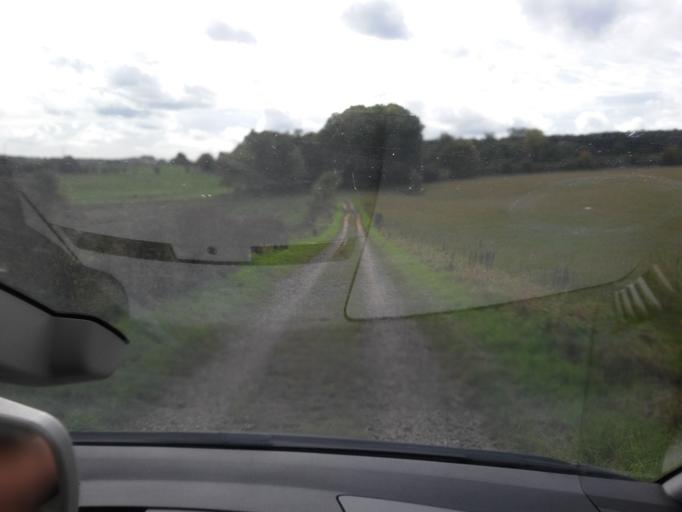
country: BE
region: Wallonia
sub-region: Province du Luxembourg
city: Arlon
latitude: 49.7050
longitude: 5.7756
